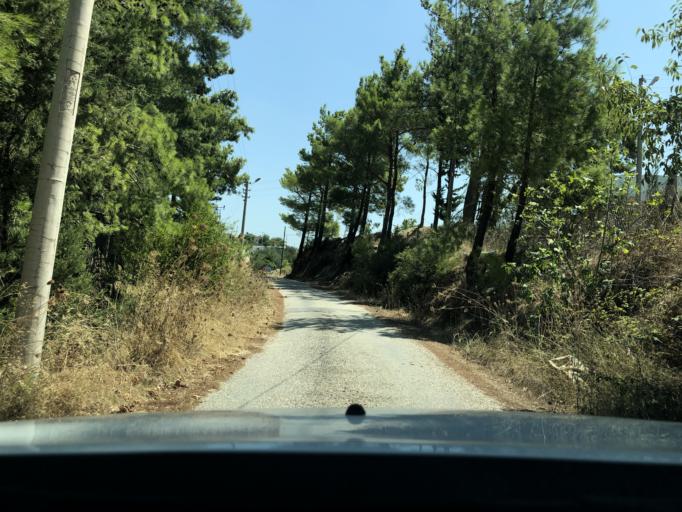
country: TR
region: Antalya
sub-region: Manavgat
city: Kizilagac
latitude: 36.8585
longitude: 31.5530
